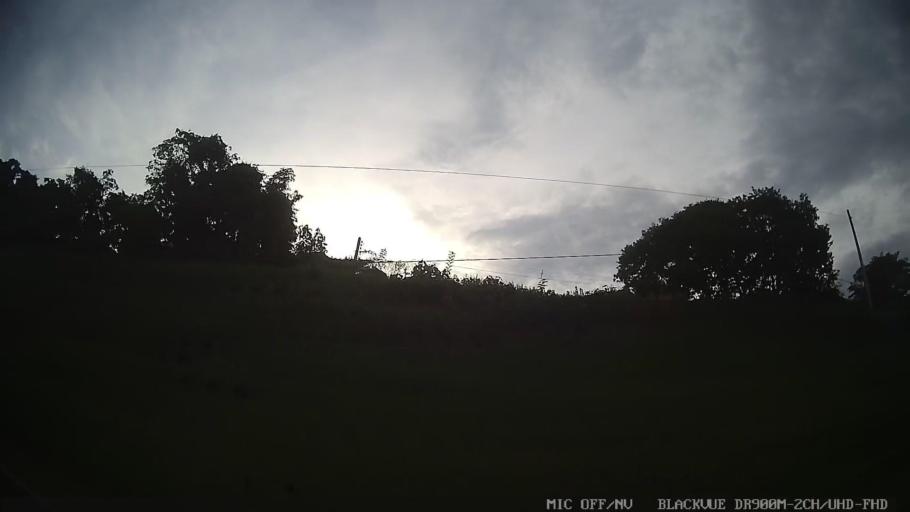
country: BR
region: Sao Paulo
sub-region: Jaguariuna
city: Jaguariuna
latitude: -22.6585
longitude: -47.0038
